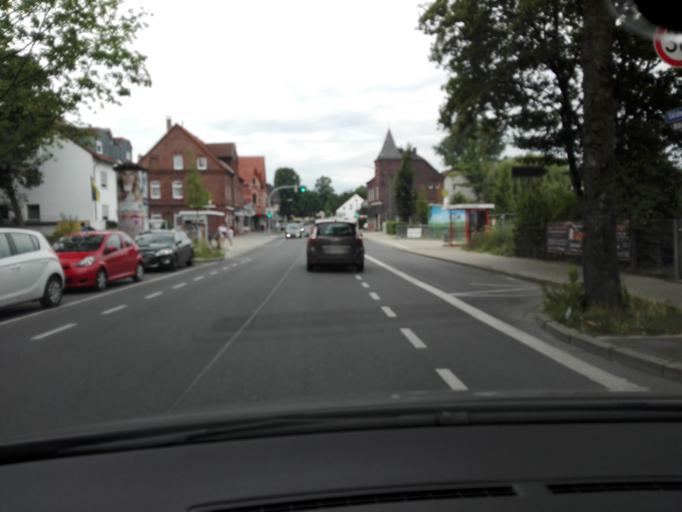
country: DE
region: North Rhine-Westphalia
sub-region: Regierungsbezirk Arnsberg
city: Holzwickede
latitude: 51.4997
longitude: 7.5874
